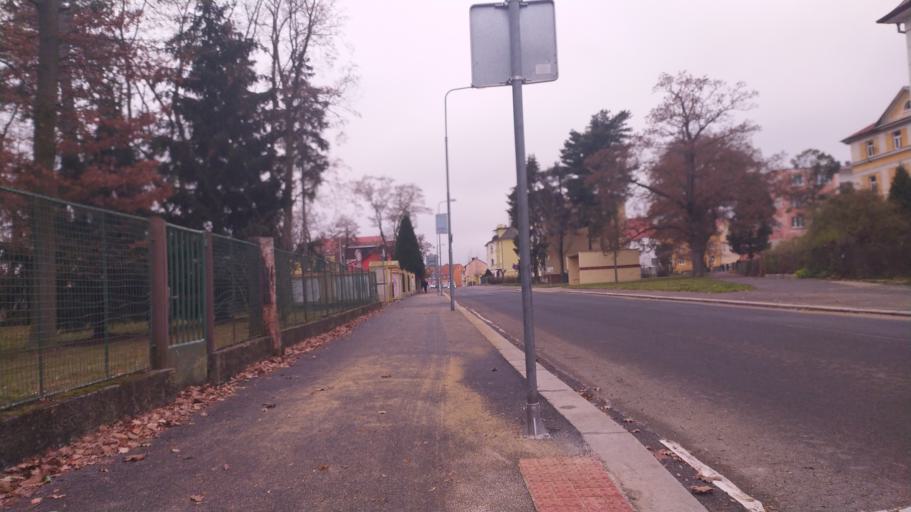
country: CZ
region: Karlovarsky
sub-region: Okres Cheb
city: Frantiskovy Lazne
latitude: 50.1240
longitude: 12.3502
